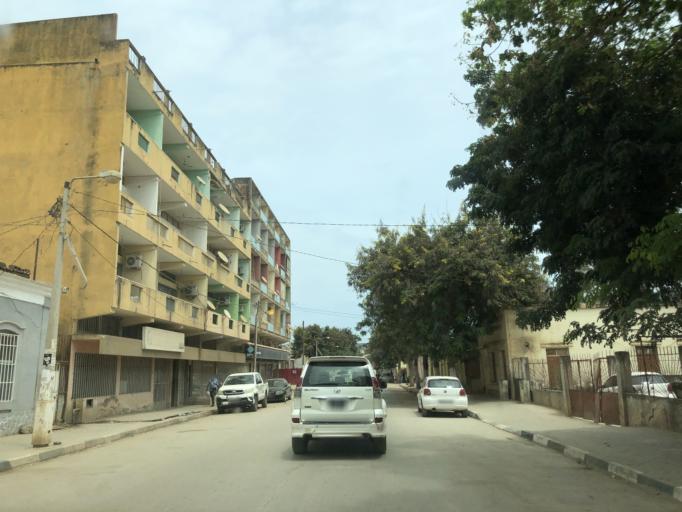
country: AO
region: Cuanza Sul
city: Sumbe
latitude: -11.2005
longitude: 13.8420
